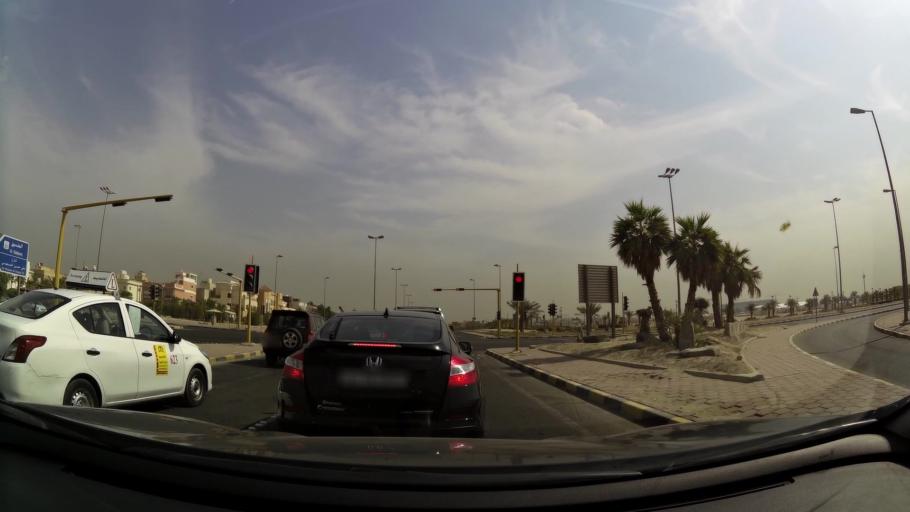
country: KW
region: Al Farwaniyah
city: Janub as Surrah
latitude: 29.2900
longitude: 48.0024
